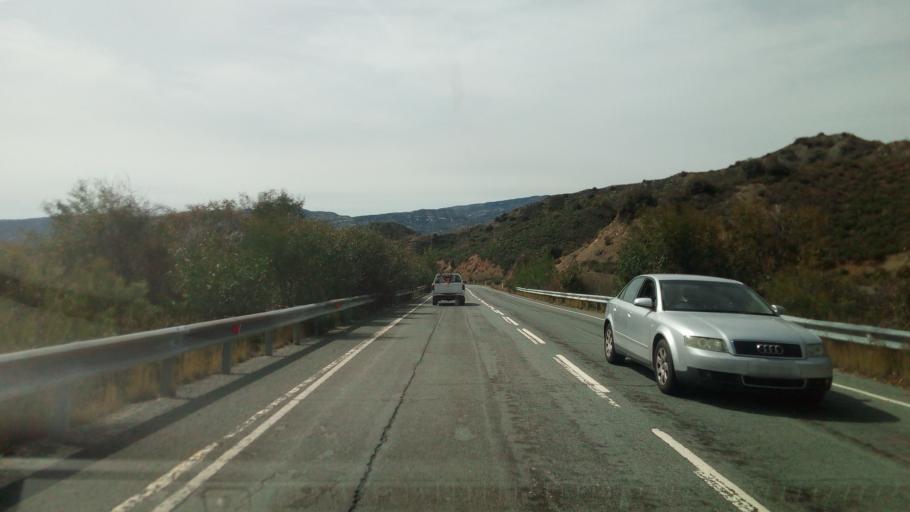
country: CY
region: Limassol
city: Pelendri
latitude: 34.8733
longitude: 32.9336
